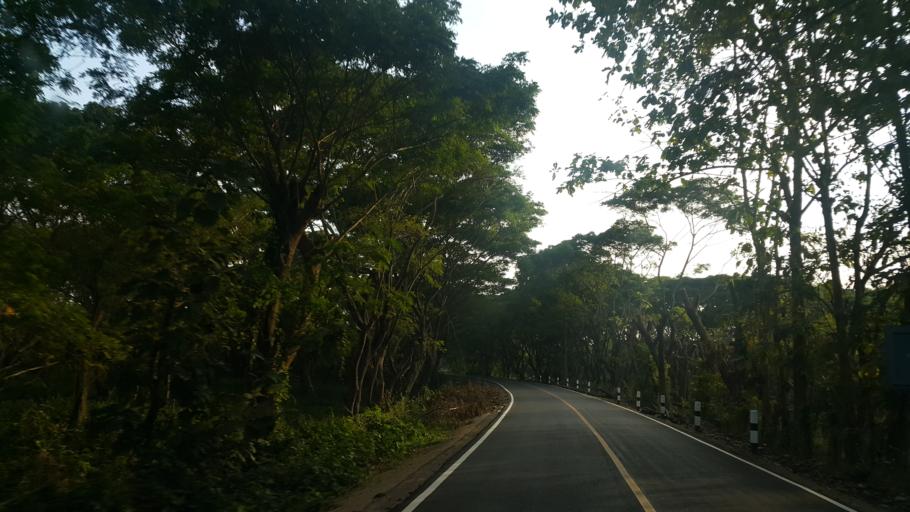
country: TH
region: Lampang
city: Sop Prap
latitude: 17.9372
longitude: 99.3406
